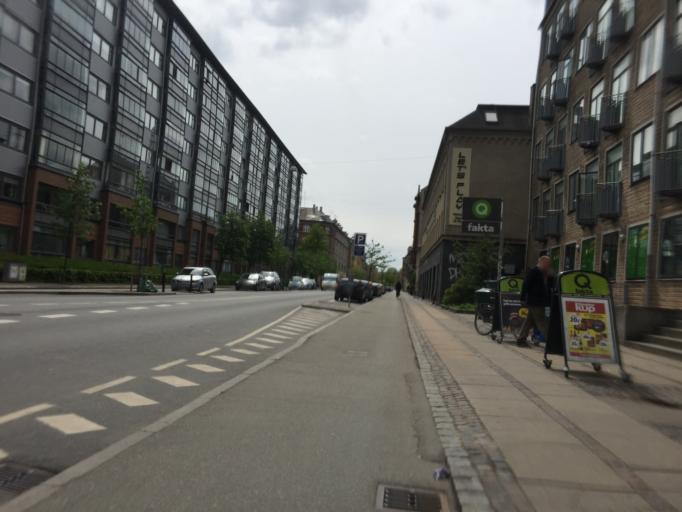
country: DK
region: Capital Region
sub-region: Frederiksberg Kommune
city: Frederiksberg
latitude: 55.6905
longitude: 12.5300
